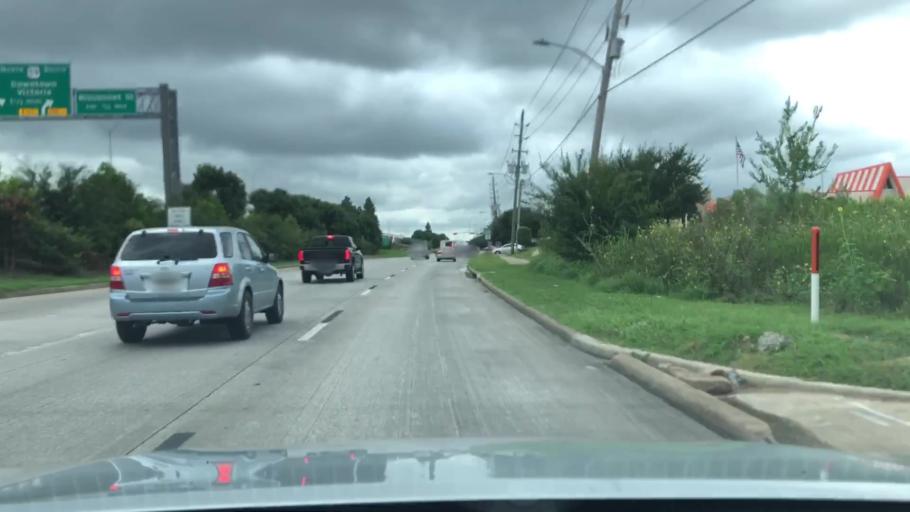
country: US
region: Texas
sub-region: Fort Bend County
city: Meadows Place
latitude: 29.6918
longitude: -95.5575
